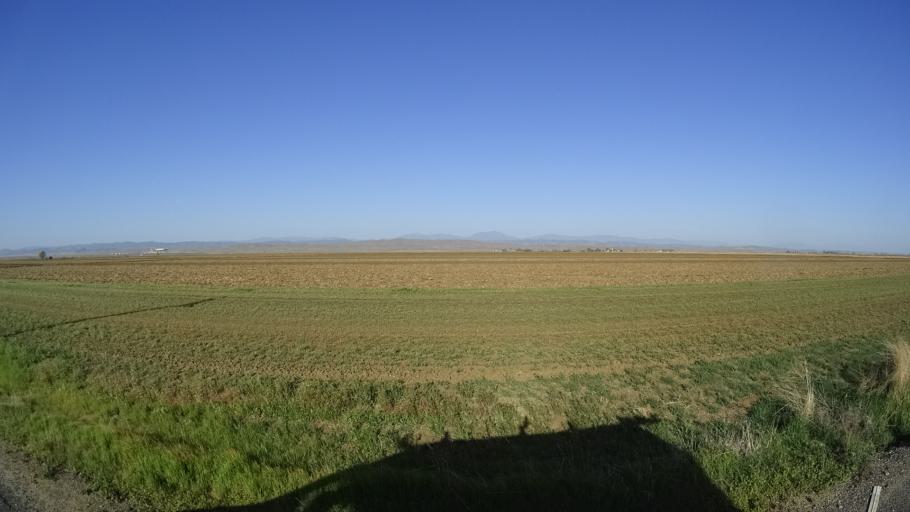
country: US
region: California
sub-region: Colusa County
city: Maxwell
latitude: 39.3900
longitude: -122.2299
